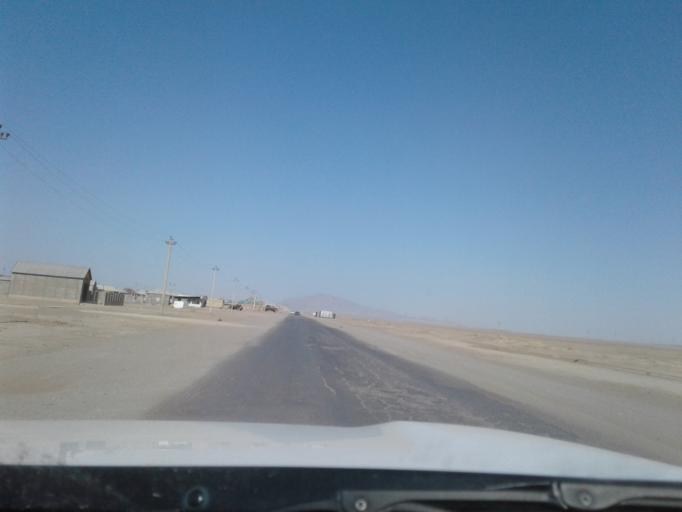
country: TM
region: Balkan
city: Gumdag
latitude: 39.1961
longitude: 54.5969
